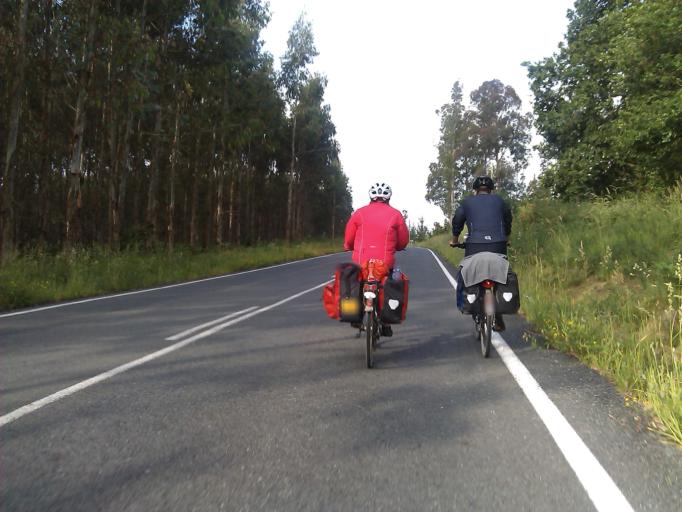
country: ES
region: Galicia
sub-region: Provincia da Coruna
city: Santiso
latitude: 42.8881
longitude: -8.0861
